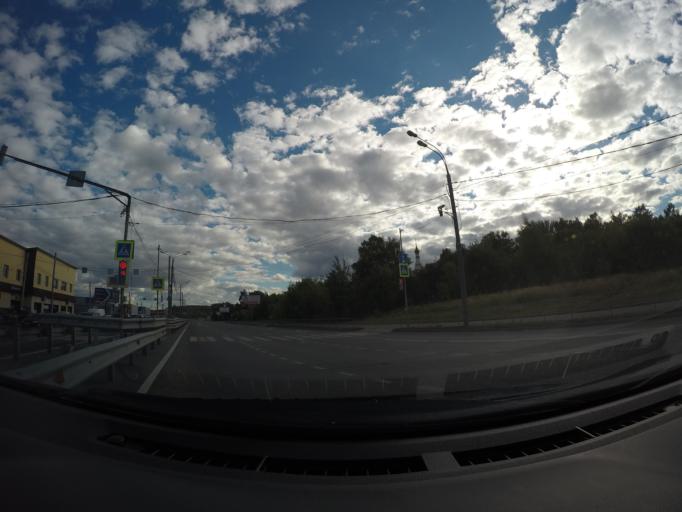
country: RU
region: Moskovskaya
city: Dolgoprudnyy
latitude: 55.9187
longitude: 37.4942
